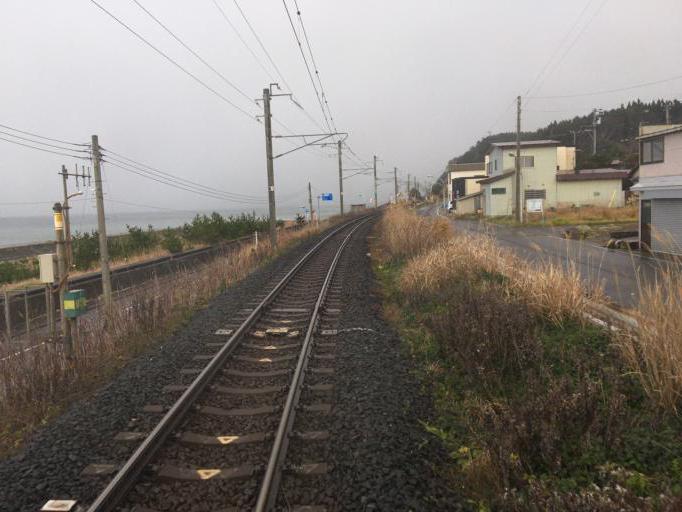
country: JP
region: Aomori
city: Aomori Shi
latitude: 41.0349
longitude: 140.6456
